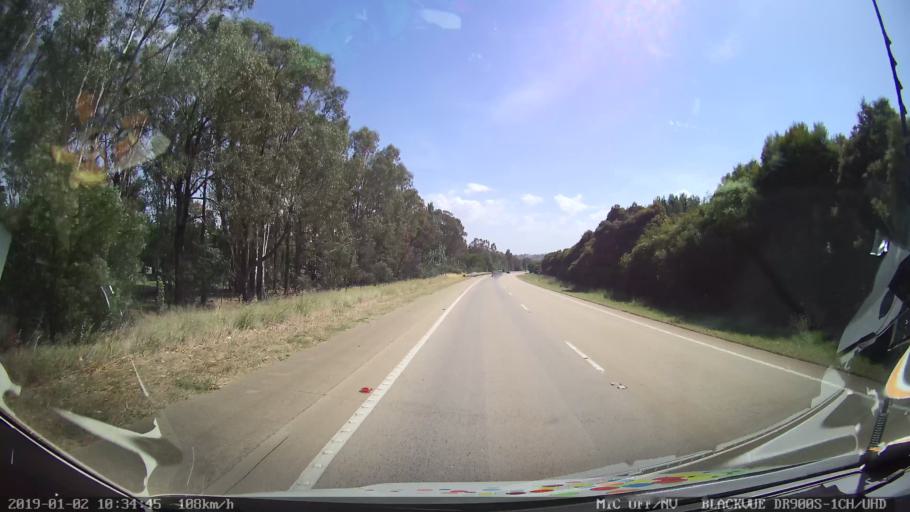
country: AU
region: New South Wales
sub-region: Gundagai
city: Gundagai
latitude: -34.8570
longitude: 148.2876
